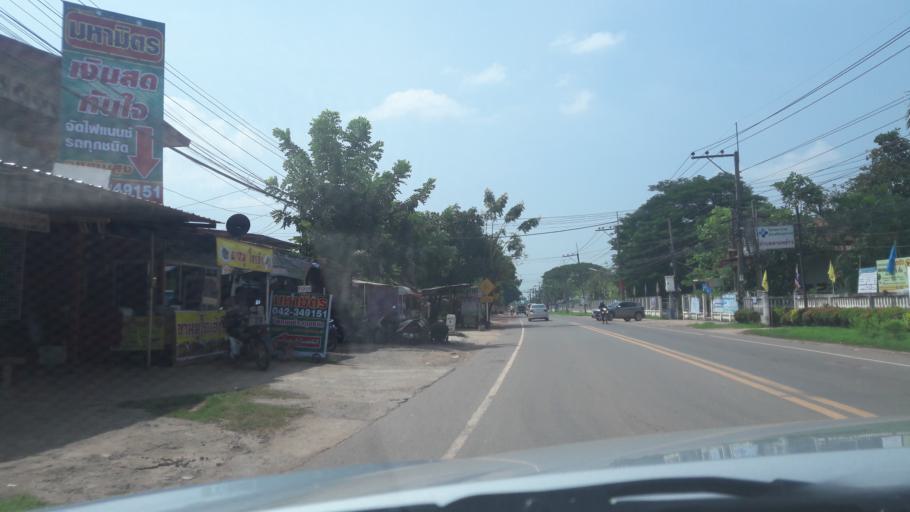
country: TH
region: Changwat Udon Thani
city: Udon Thani
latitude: 17.4446
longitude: 102.8741
